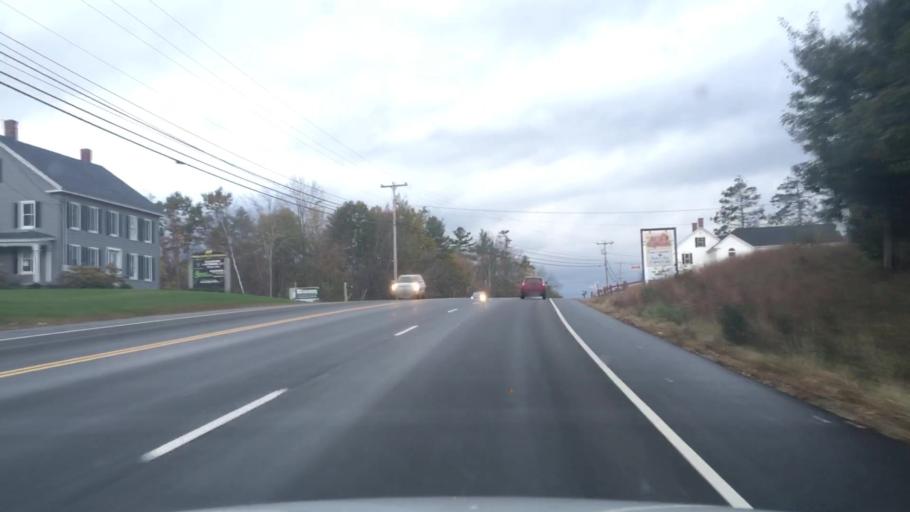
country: US
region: New Hampshire
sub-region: Merrimack County
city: Chichester
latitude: 43.2384
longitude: -71.3929
